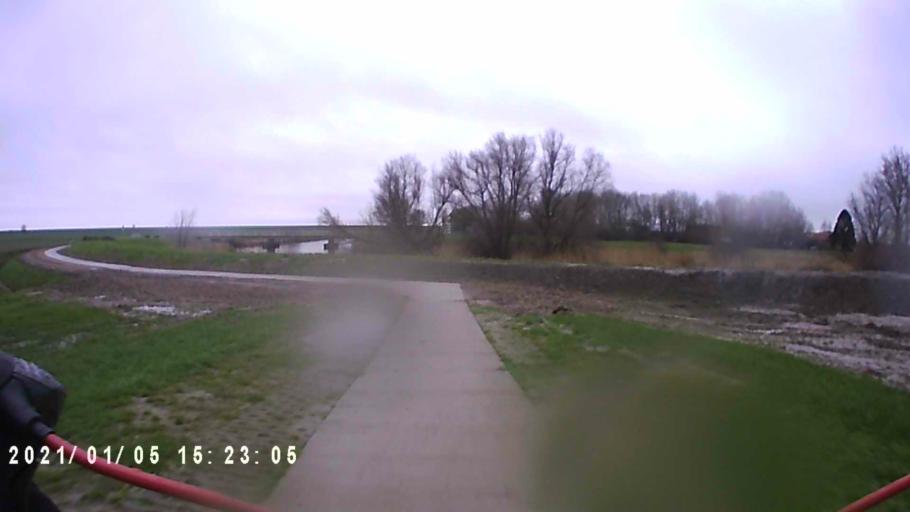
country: DE
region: Lower Saxony
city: Bunde
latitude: 53.2271
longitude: 7.2073
